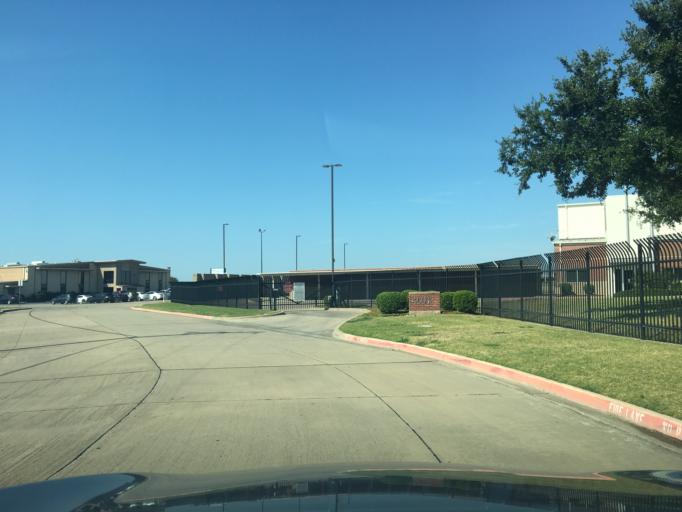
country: US
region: Texas
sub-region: Dallas County
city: Addison
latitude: 32.9656
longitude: -96.8318
